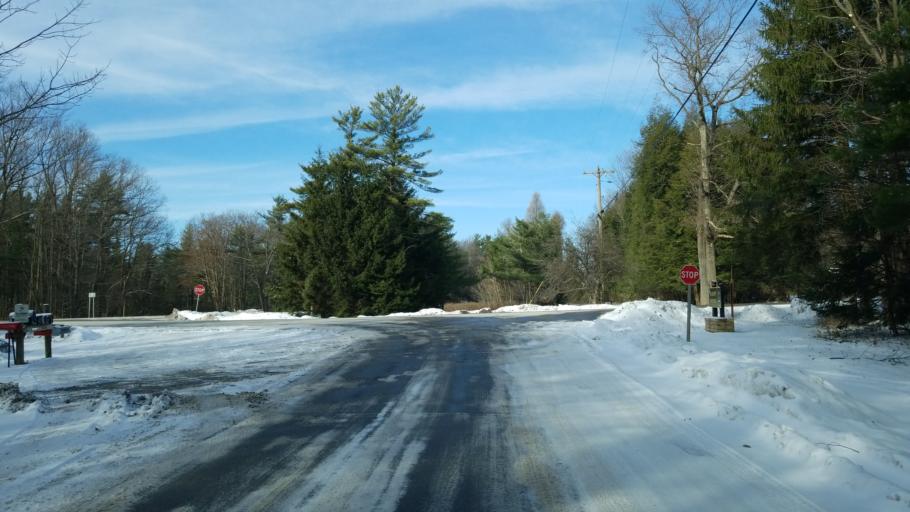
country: US
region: Pennsylvania
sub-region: Clearfield County
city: Clearfield
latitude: 41.1230
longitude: -78.5333
